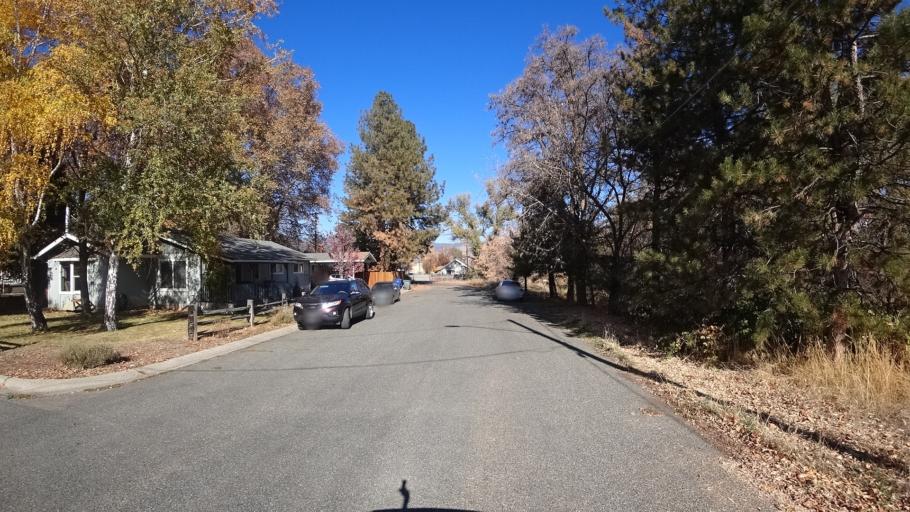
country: US
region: California
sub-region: Siskiyou County
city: Yreka
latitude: 41.7366
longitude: -122.6323
